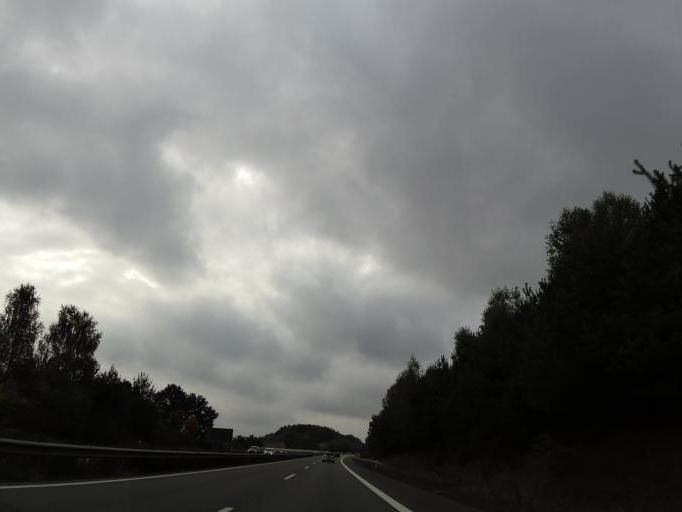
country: DE
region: Rheinland-Pfalz
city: Sembach
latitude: 49.5189
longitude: 7.8461
